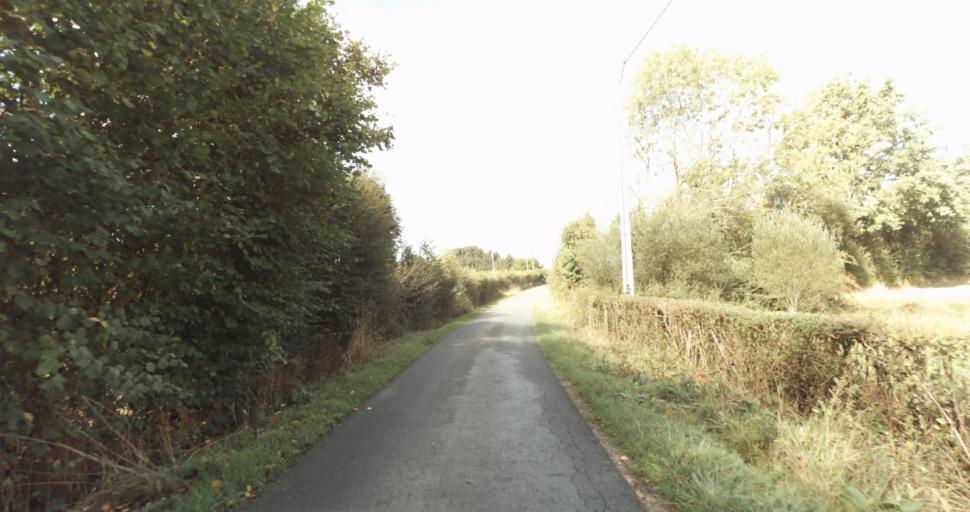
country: FR
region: Lower Normandy
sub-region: Departement de l'Orne
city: Vimoutiers
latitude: 48.9501
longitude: 0.3143
